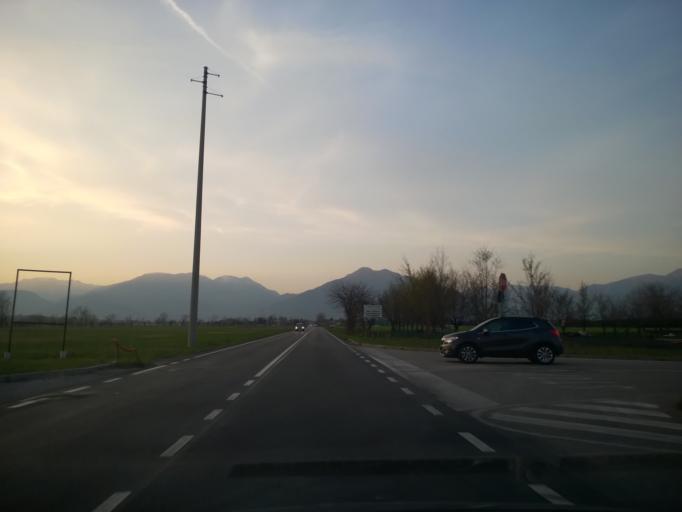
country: IT
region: Veneto
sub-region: Provincia di Vicenza
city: Marano Vicentino
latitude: 45.6805
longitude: 11.4537
